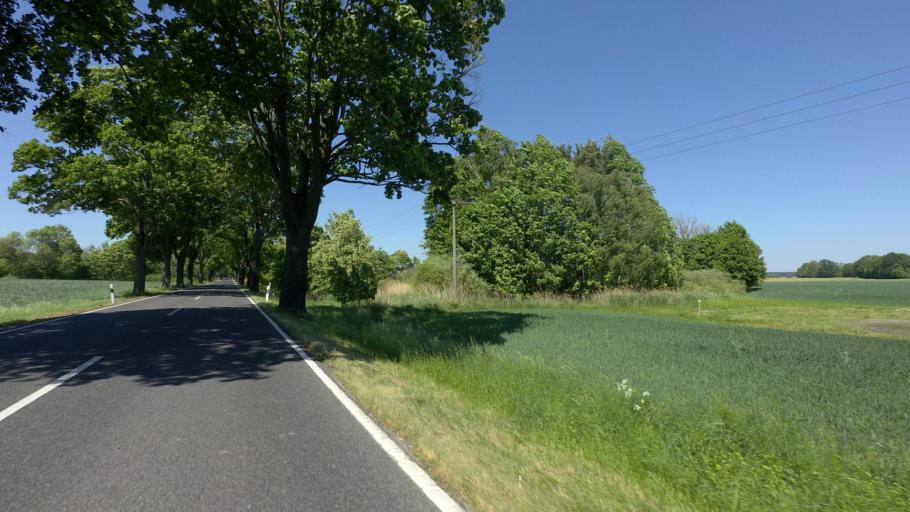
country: DE
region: Brandenburg
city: Lieberose
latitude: 51.9692
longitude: 14.3107
